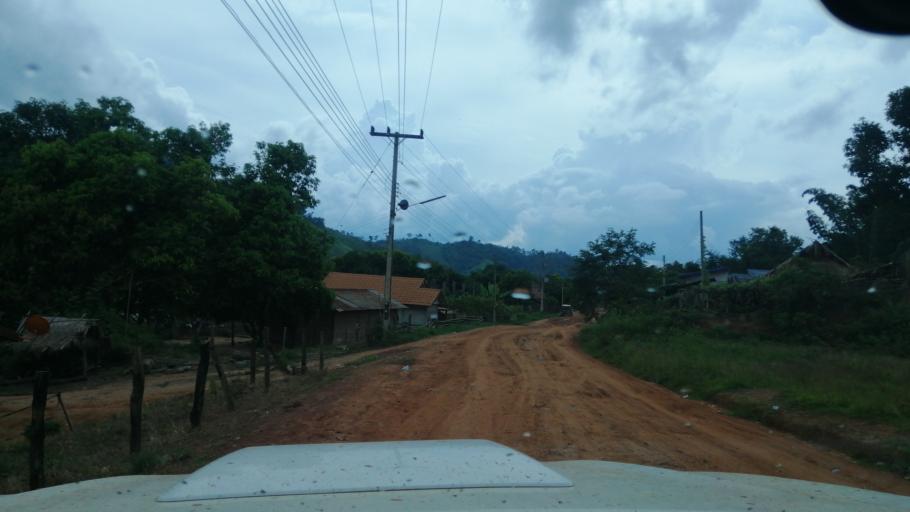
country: TH
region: Nan
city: Mae Charim
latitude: 18.7981
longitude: 101.3802
